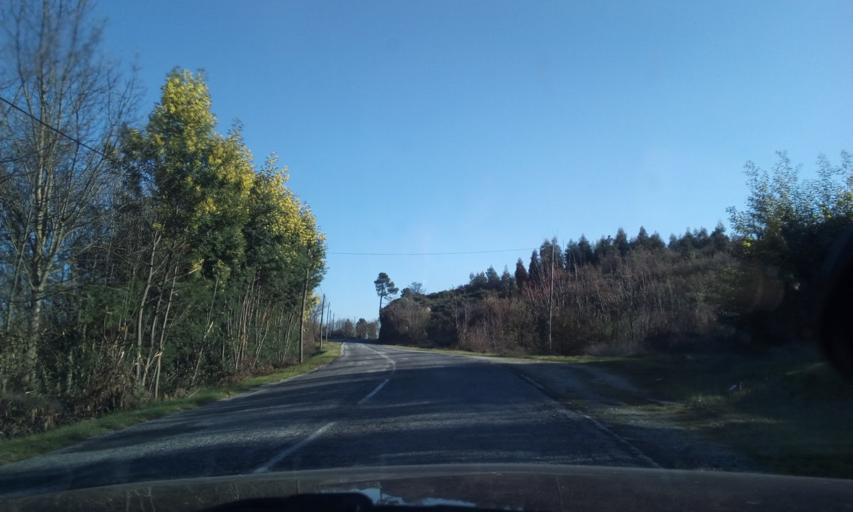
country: PT
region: Guarda
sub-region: Fornos de Algodres
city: Fornos de Algodres
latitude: 40.6250
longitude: -7.4735
